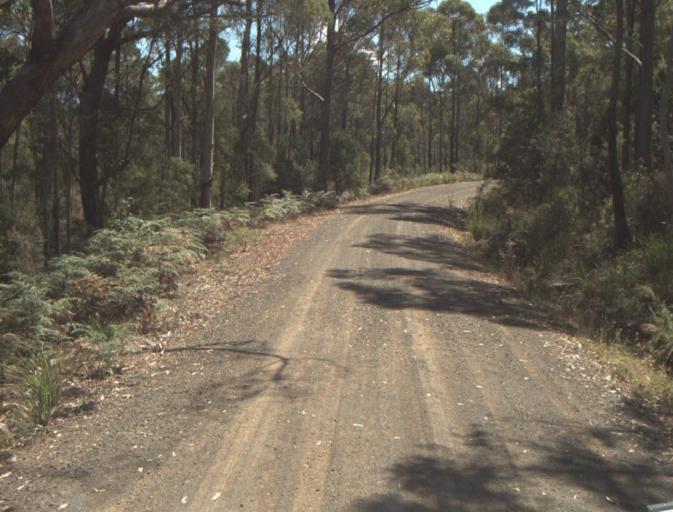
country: AU
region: Tasmania
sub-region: Launceston
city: Mayfield
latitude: -41.2781
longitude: 147.1163
